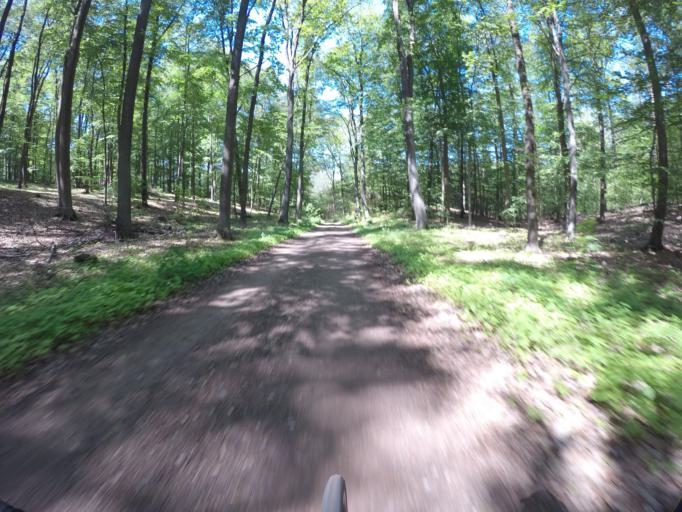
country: DE
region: Brandenburg
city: Potsdam
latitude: 52.4543
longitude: 13.0665
